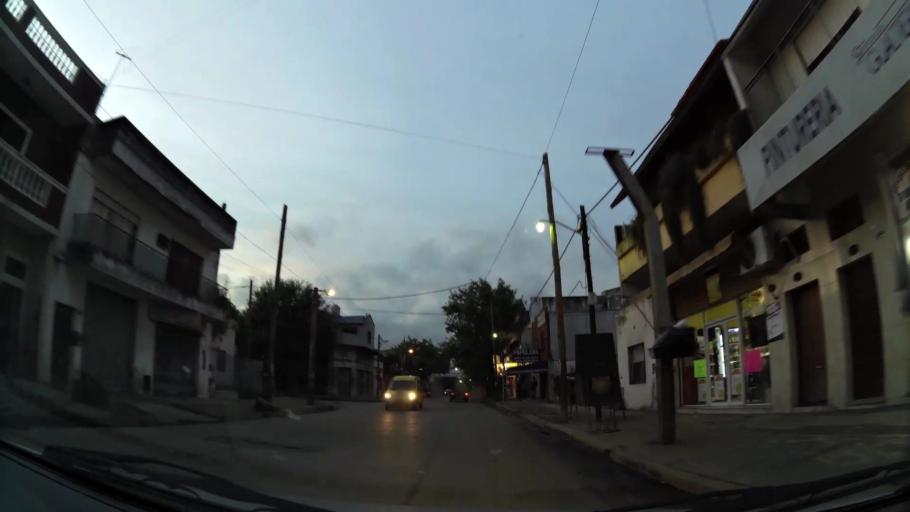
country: AR
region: Buenos Aires
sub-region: Partido de Lomas de Zamora
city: Lomas de Zamora
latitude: -34.7443
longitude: -58.3683
